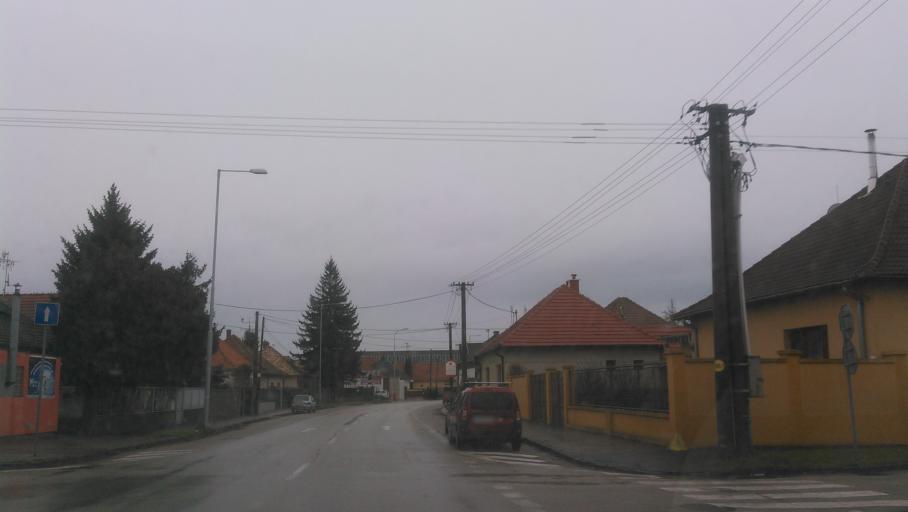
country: SK
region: Nitriansky
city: Sellye
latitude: 48.1553
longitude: 17.8659
